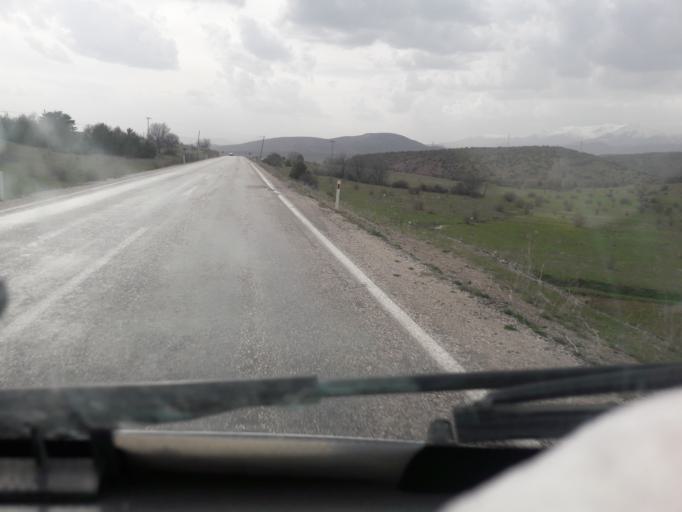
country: TR
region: Gumushane
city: Evren
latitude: 40.1707
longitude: 39.2470
